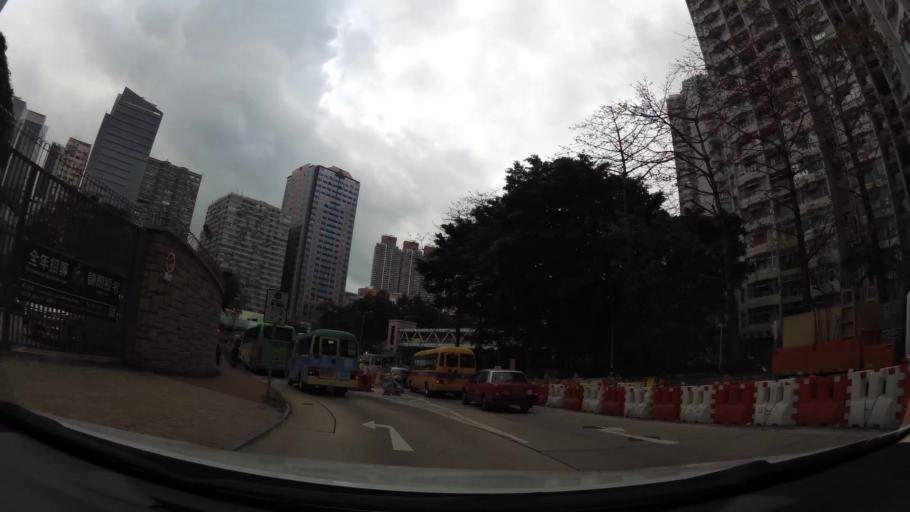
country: HK
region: Wong Tai Sin
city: Wong Tai Sin
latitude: 22.3391
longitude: 114.1960
